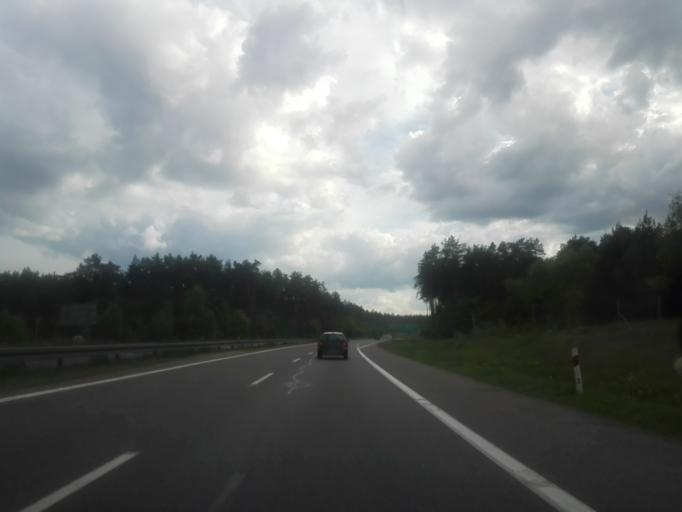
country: PL
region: Masovian Voivodeship
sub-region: Powiat ostrowski
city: Ostrow Mazowiecka
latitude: 52.7893
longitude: 21.8653
